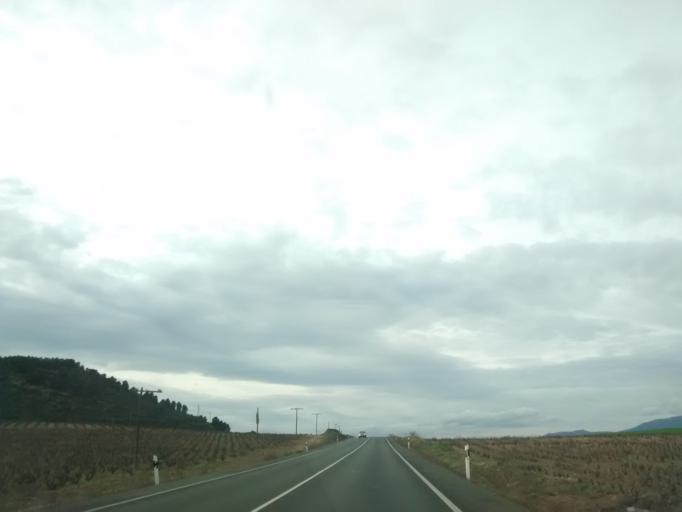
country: ES
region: La Rioja
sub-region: Provincia de La Rioja
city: Torremontalbo
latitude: 42.5040
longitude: -2.6900
